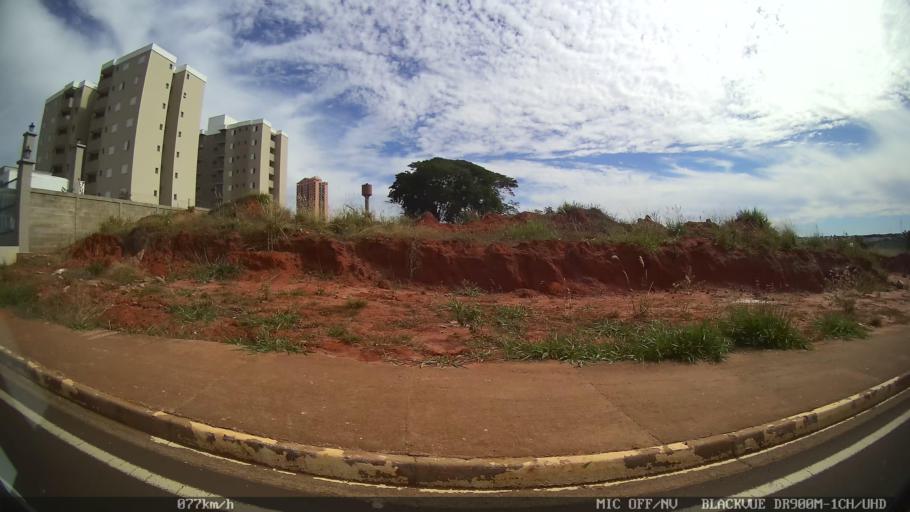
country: BR
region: Sao Paulo
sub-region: Catanduva
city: Catanduva
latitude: -21.1535
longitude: -48.9539
